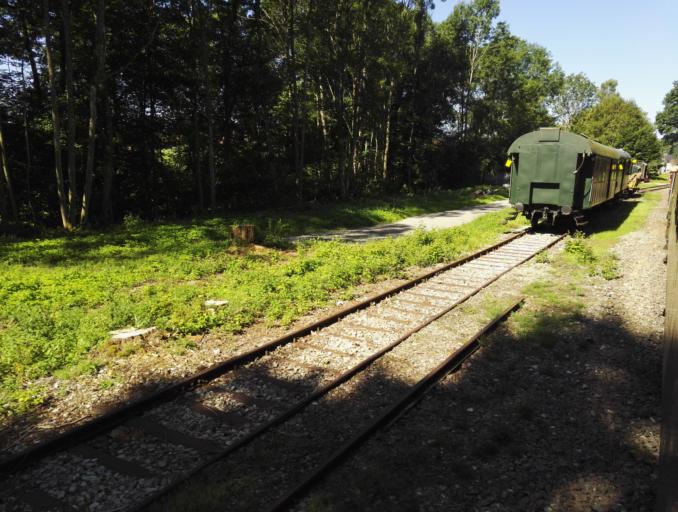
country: DE
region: Baden-Wuerttemberg
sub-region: Regierungsbezirk Stuttgart
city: Welzheim
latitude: 48.8597
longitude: 9.6326
